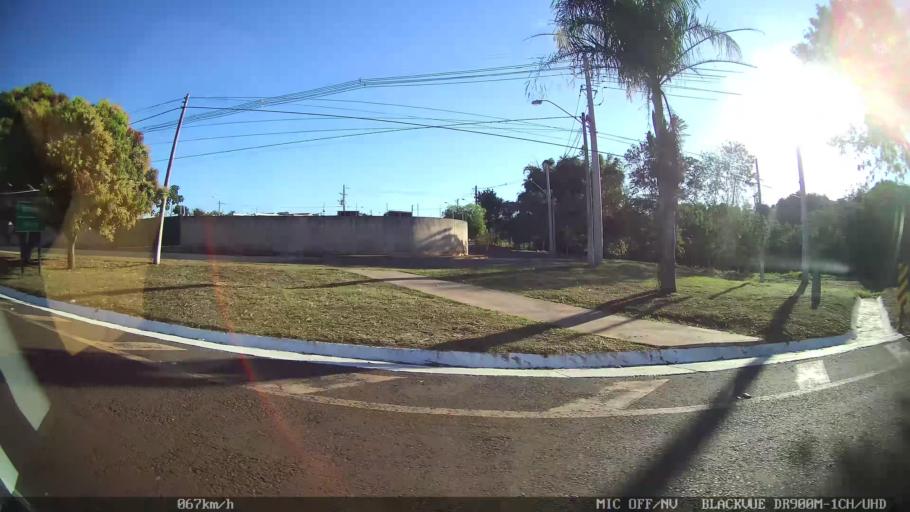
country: BR
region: Sao Paulo
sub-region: Guapiacu
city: Guapiacu
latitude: -20.7871
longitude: -49.2235
